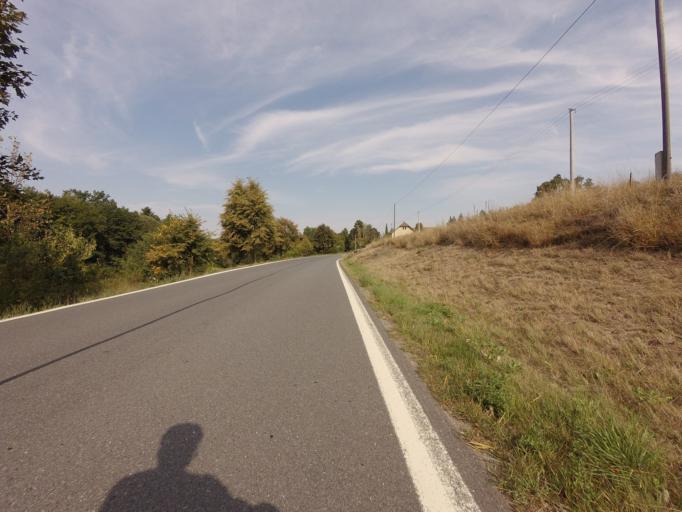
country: CZ
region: Central Bohemia
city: Petrovice
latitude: 49.5412
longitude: 14.3491
